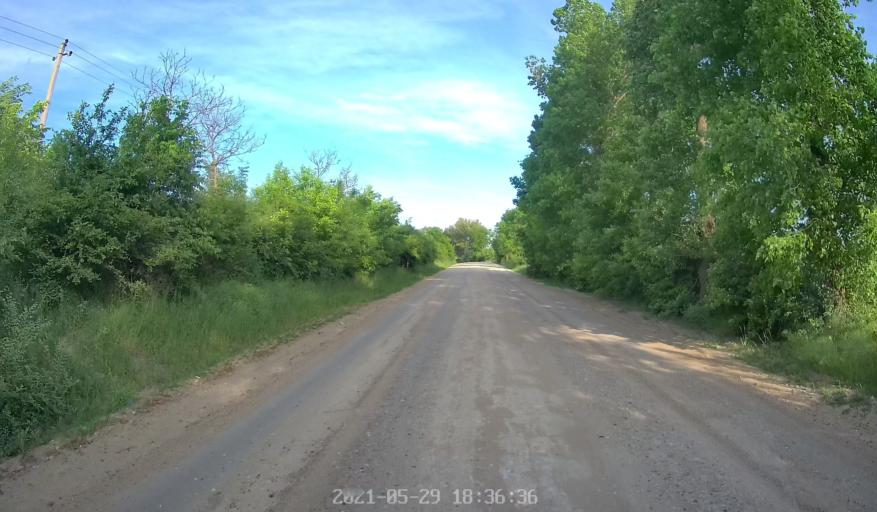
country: MD
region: Chisinau
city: Singera
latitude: 46.8062
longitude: 28.9255
